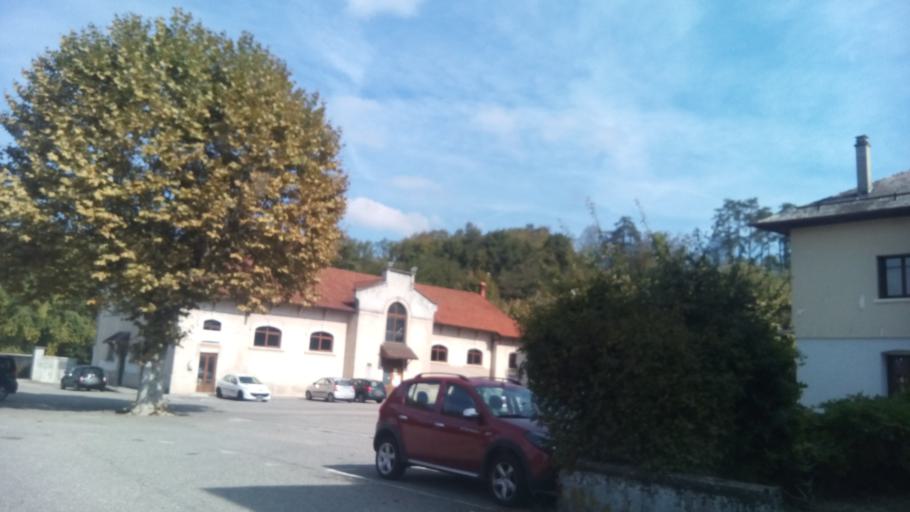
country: FR
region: Rhone-Alpes
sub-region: Departement de la Savoie
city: Les Echelles
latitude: 45.4376
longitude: 5.7525
